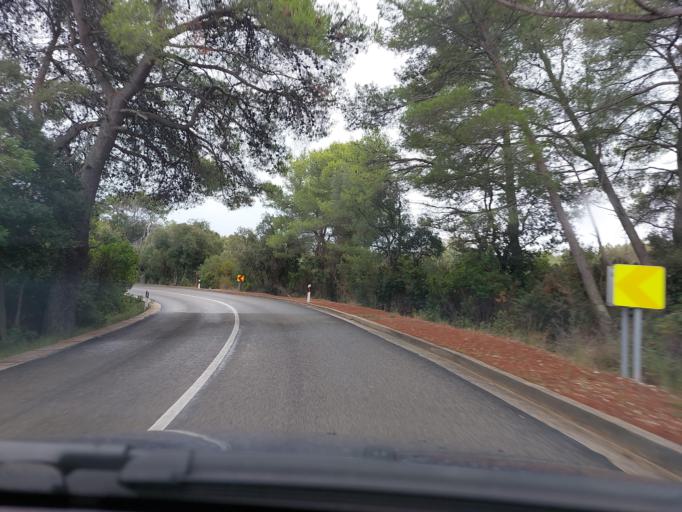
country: HR
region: Dubrovacko-Neretvanska
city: Smokvica
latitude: 42.7663
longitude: 16.8722
